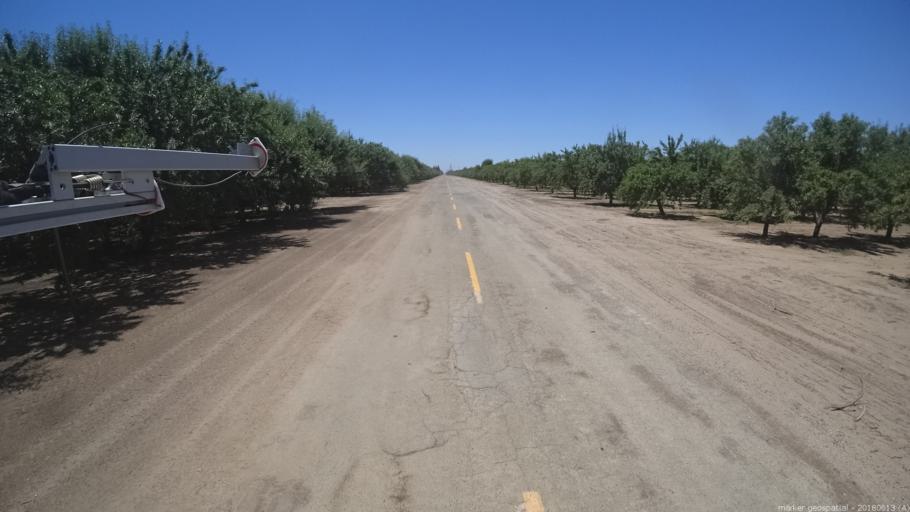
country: US
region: California
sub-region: Madera County
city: Chowchilla
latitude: 37.0328
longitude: -120.2762
